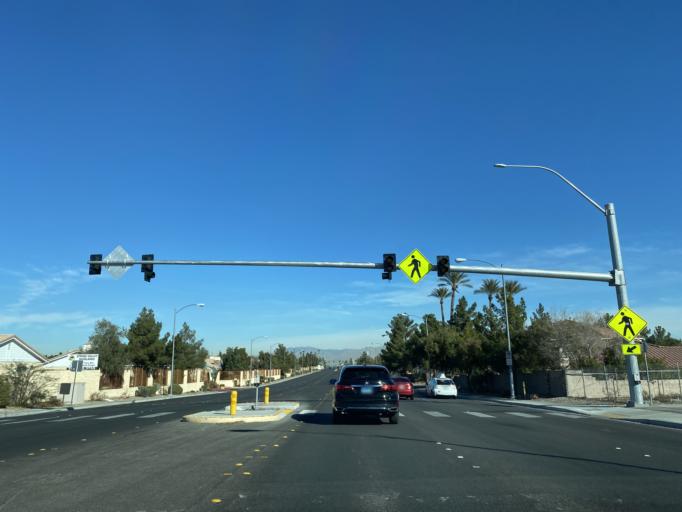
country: US
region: Nevada
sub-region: Clark County
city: Spring Valley
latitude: 36.0888
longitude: -115.2252
